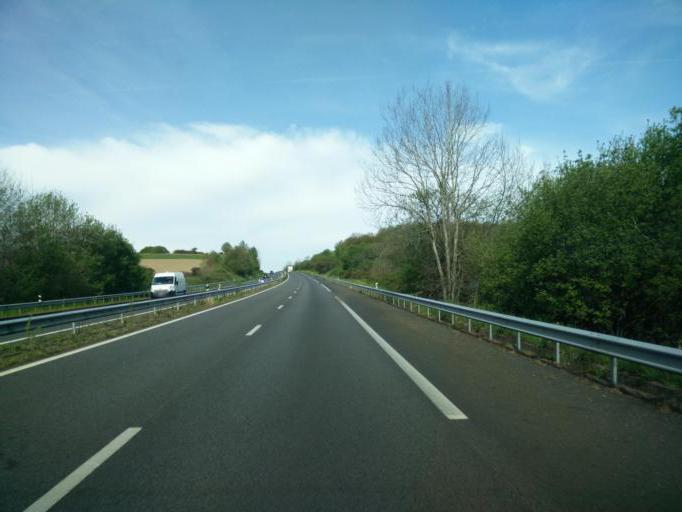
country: FR
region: Brittany
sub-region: Departement d'Ille-et-Vilaine
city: Pleine-Fougeres
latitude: 48.5658
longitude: -1.5648
